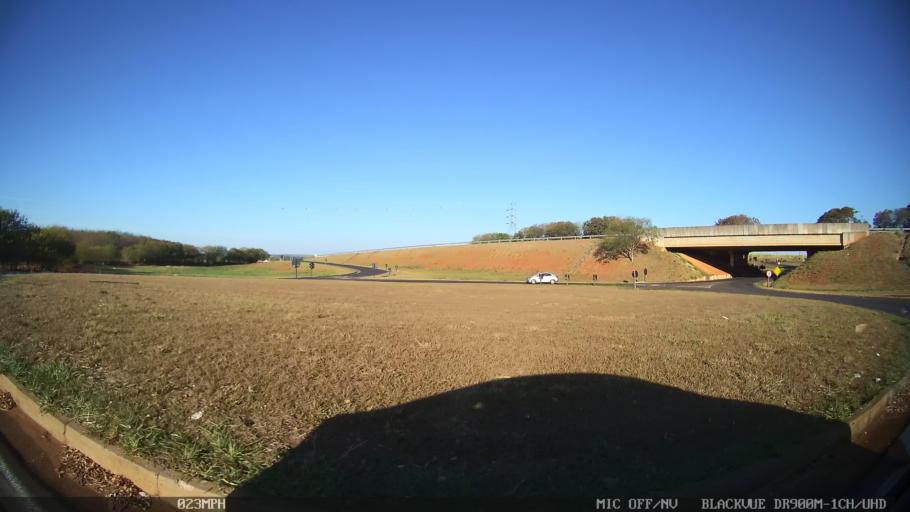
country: BR
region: Sao Paulo
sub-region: Guapiacu
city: Guapiacu
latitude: -20.7726
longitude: -49.2256
